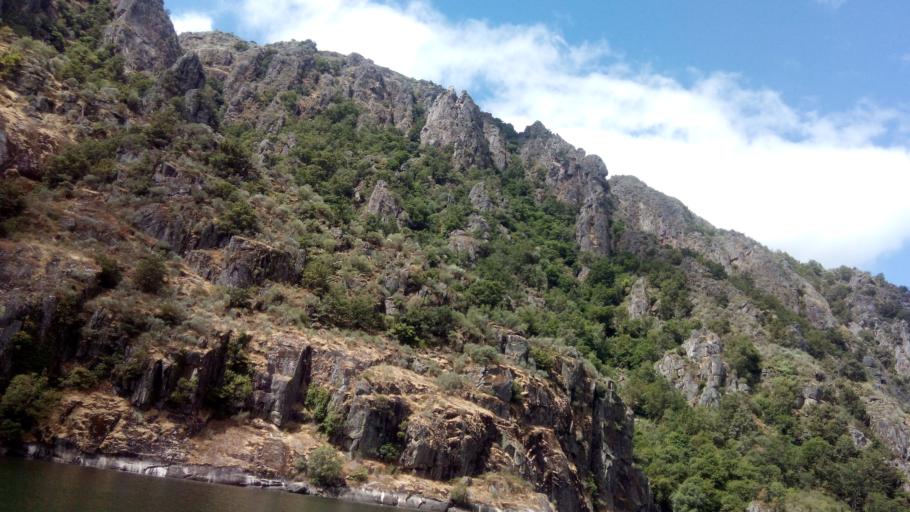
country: ES
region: Galicia
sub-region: Provincia de Lugo
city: Sober
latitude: 42.3863
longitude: -7.6197
